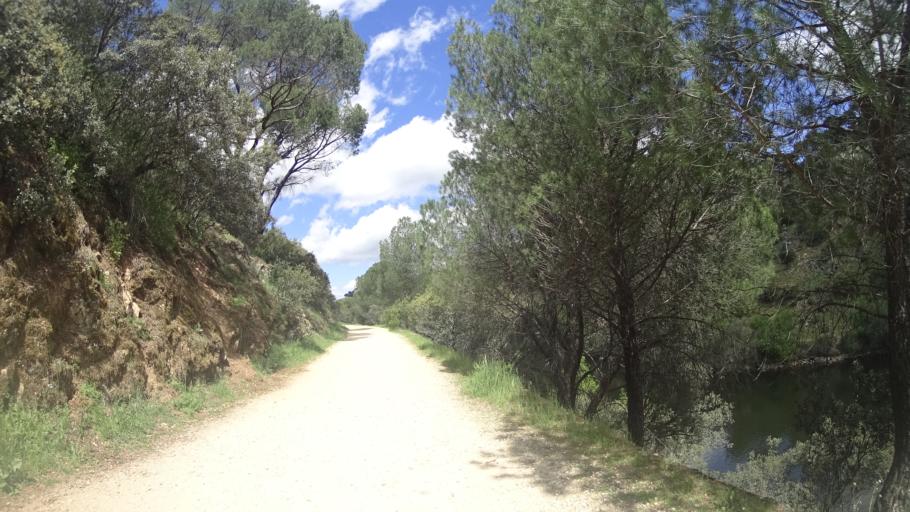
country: ES
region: Madrid
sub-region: Provincia de Madrid
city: Pelayos de la Presa
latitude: 40.3655
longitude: -4.2988
